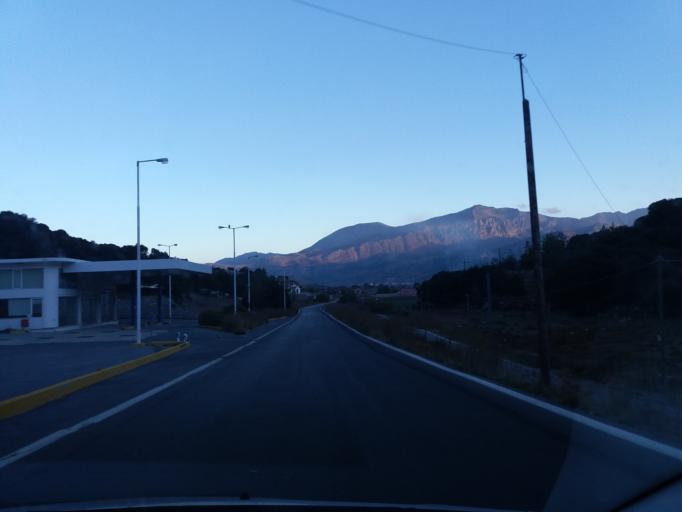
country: GR
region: Crete
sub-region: Nomos Irakleiou
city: Mokhos
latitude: 35.1998
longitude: 25.4603
